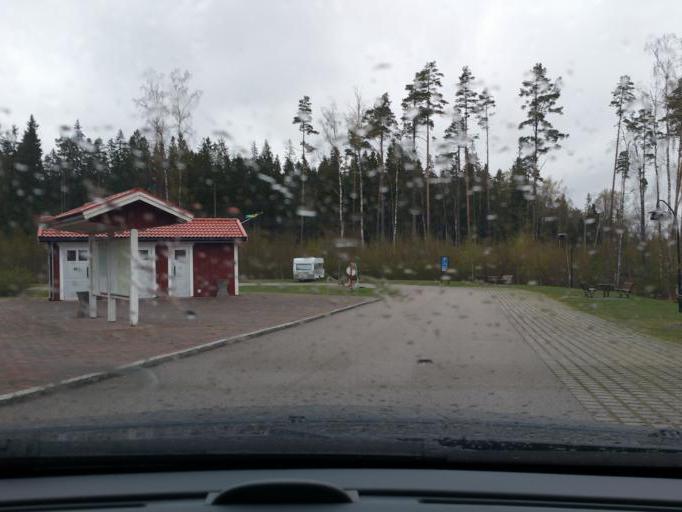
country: SE
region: Kronoberg
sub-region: Vaxjo Kommun
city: Lammhult
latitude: 57.1373
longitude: 14.6086
